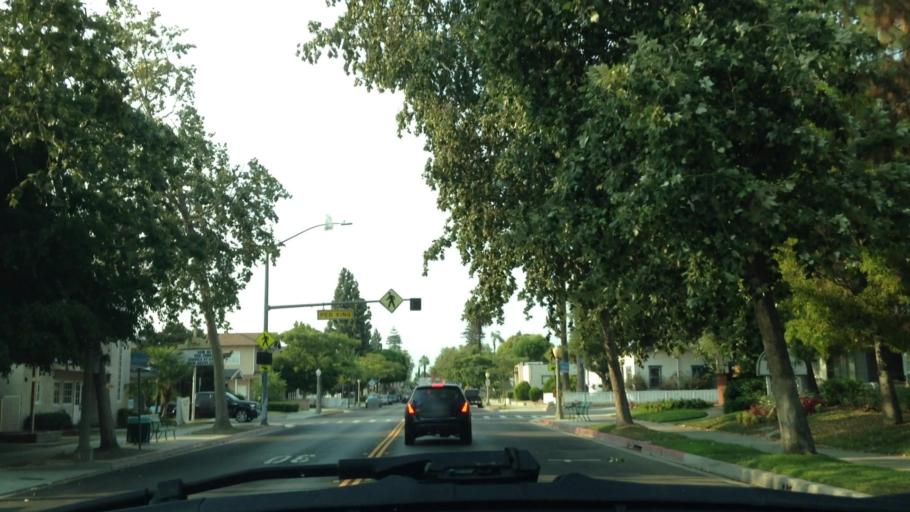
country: US
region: California
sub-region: Orange County
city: Orange
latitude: 33.7836
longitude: -117.8531
